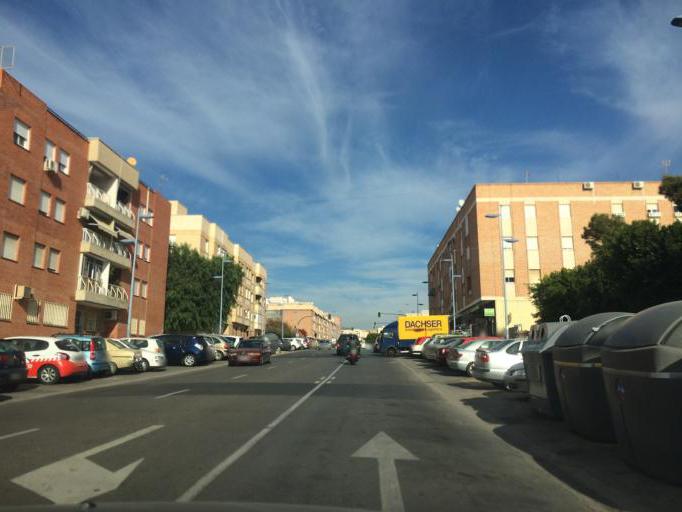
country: ES
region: Andalusia
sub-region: Provincia de Almeria
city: Almeria
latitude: 36.8399
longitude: -2.4495
